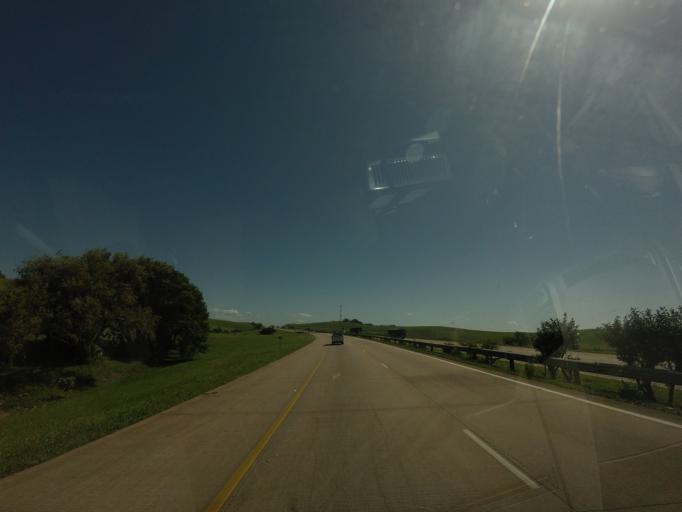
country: ZA
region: KwaZulu-Natal
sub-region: iLembe District Municipality
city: Stanger
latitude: -29.4281
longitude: 31.2731
